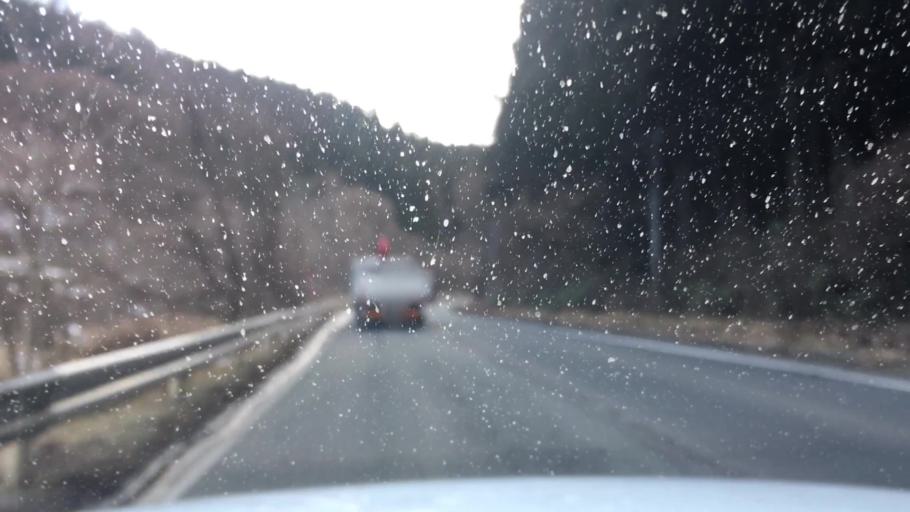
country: JP
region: Iwate
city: Morioka-shi
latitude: 39.6752
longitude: 141.2016
